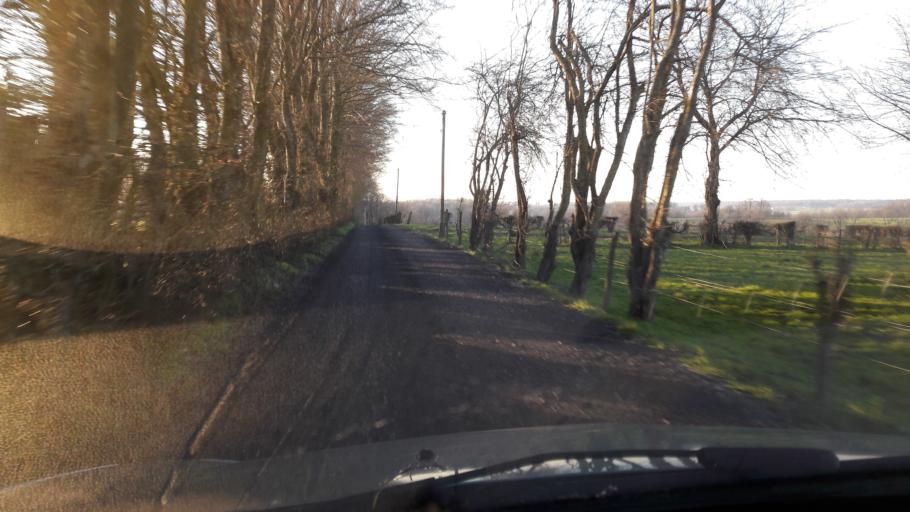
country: BE
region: Wallonia
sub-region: Province du Hainaut
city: Beaumont
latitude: 50.2457
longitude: 4.1888
